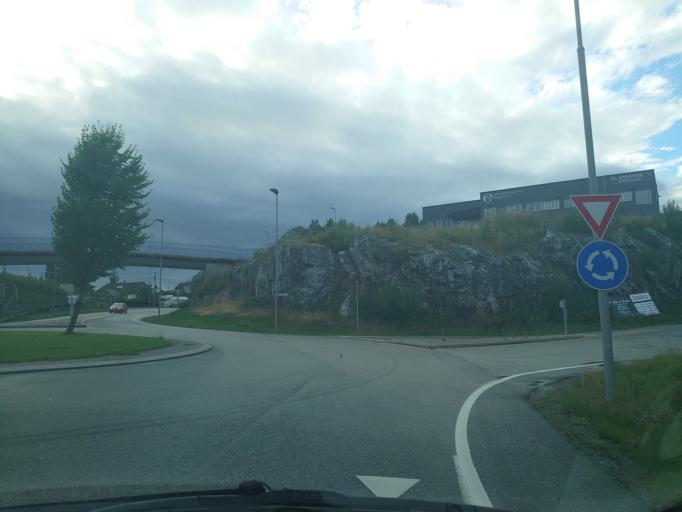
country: NO
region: Hordaland
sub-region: Lindas
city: Isdalsto
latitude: 60.5577
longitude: 5.2643
